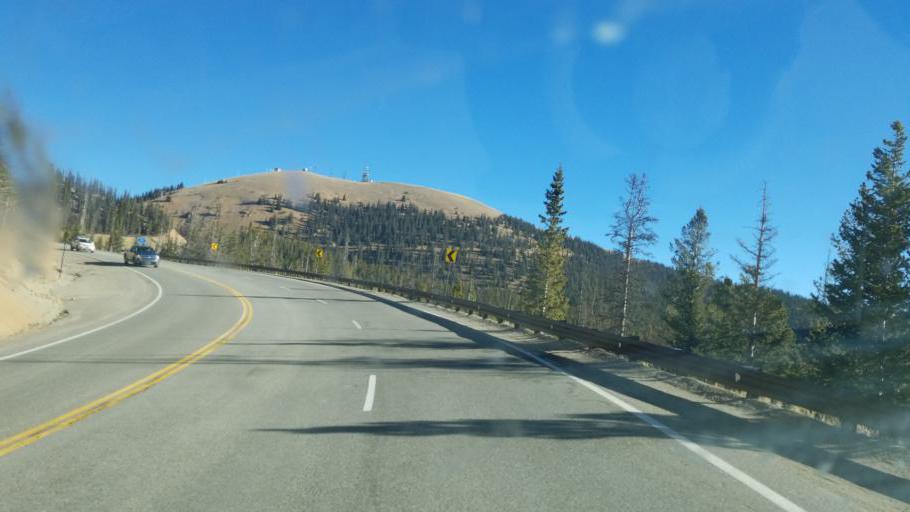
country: US
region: Colorado
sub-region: Chaffee County
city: Salida
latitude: 38.4863
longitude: -106.3290
